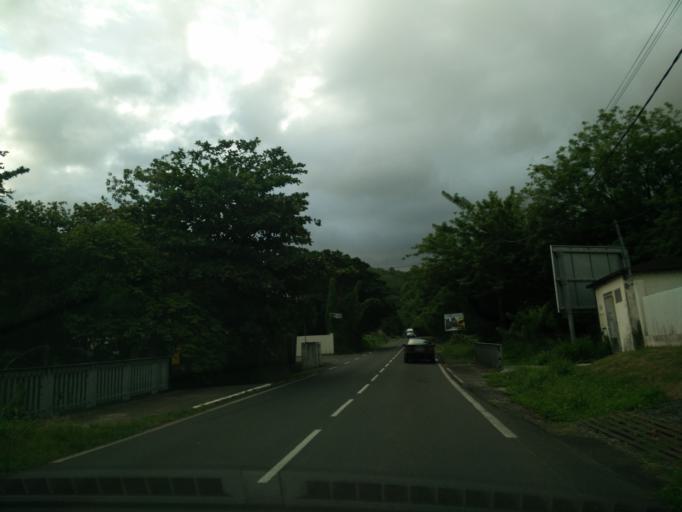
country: MQ
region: Martinique
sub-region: Martinique
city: Le Marin
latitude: 14.4714
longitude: -60.8578
